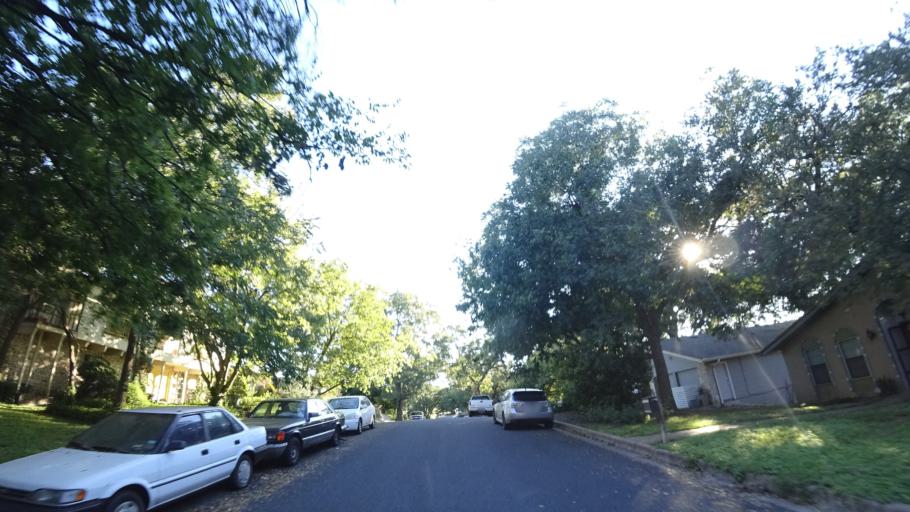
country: US
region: Texas
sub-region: Travis County
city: Austin
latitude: 30.2198
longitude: -97.7348
